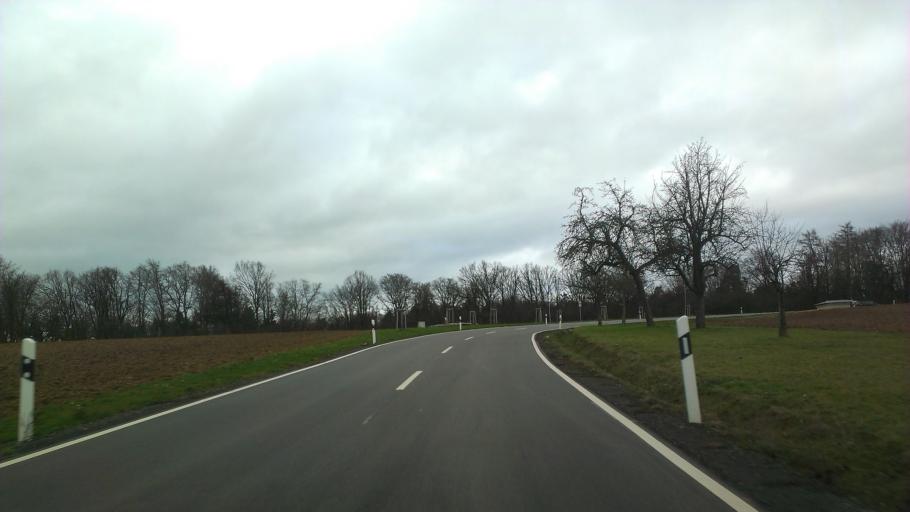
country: DE
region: Baden-Wuerttemberg
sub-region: Regierungsbezirk Stuttgart
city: Zaberfeld
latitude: 49.0811
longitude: 8.8951
